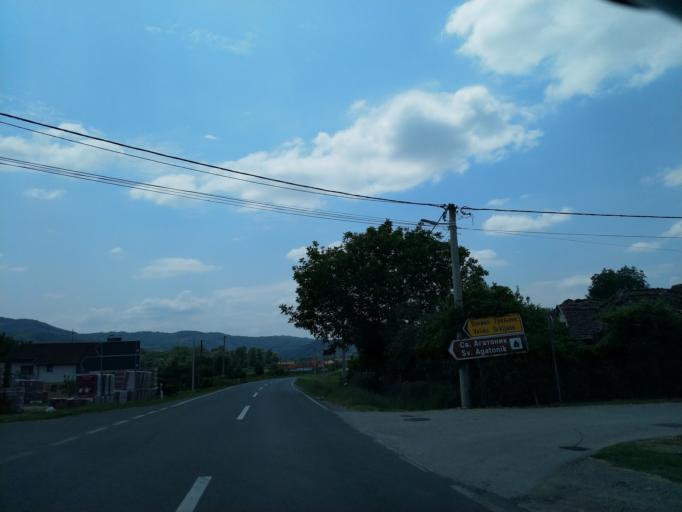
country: RS
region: Central Serbia
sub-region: Toplicki Okrug
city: Blace
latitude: 43.4426
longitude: 21.2263
